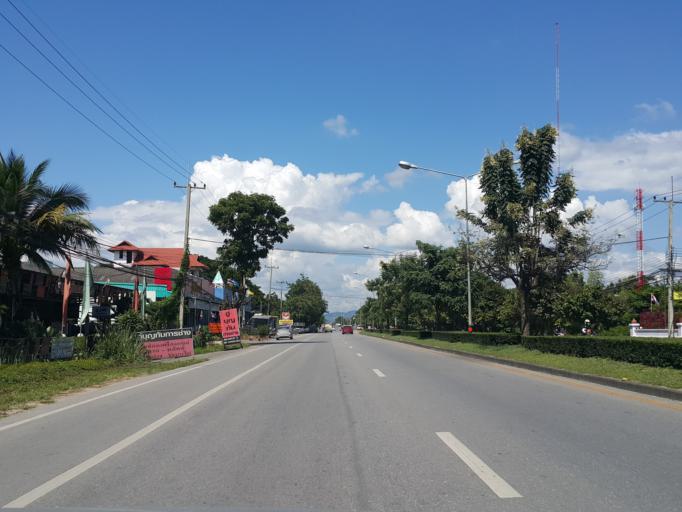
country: TH
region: Chiang Mai
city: San Sai
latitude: 18.8401
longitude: 99.0131
